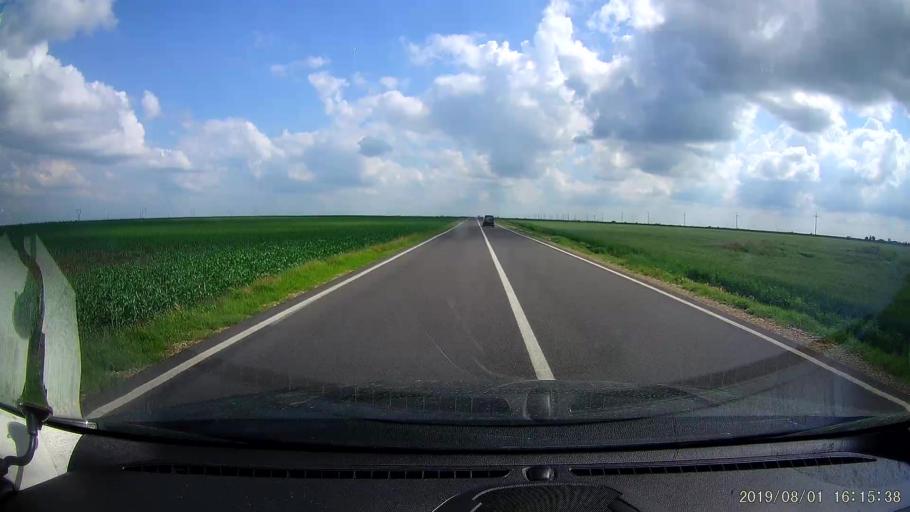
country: RO
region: Calarasi
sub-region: Comuna Stefan Voda
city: Stefan Voda
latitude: 44.3345
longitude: 27.3606
